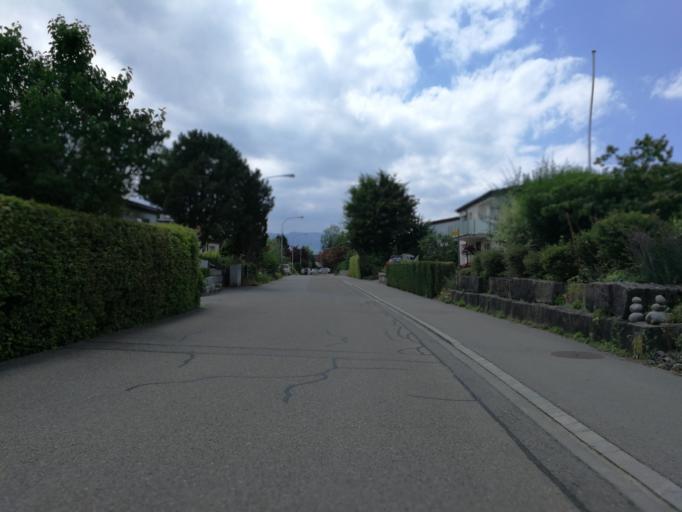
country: CH
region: Zurich
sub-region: Bezirk Hinwil
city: Wolfhausen
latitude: 47.2598
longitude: 8.7986
